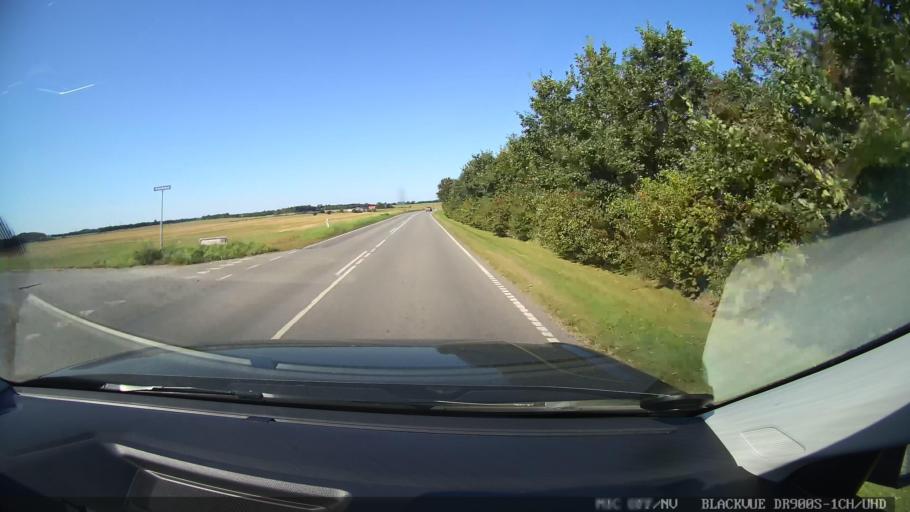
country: DK
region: Central Jutland
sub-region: Randers Kommune
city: Spentrup
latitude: 56.5324
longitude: 9.9993
